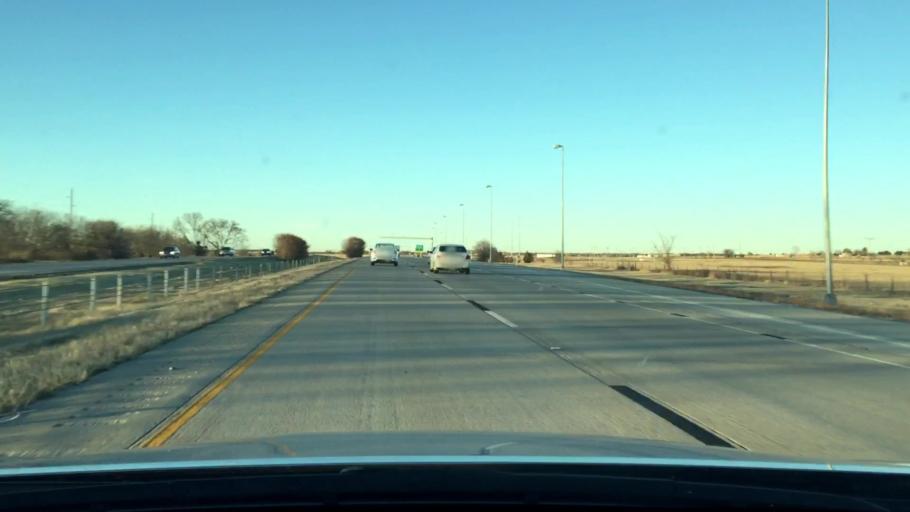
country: US
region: Oklahoma
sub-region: Love County
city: Marietta
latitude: 33.8975
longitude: -97.1344
